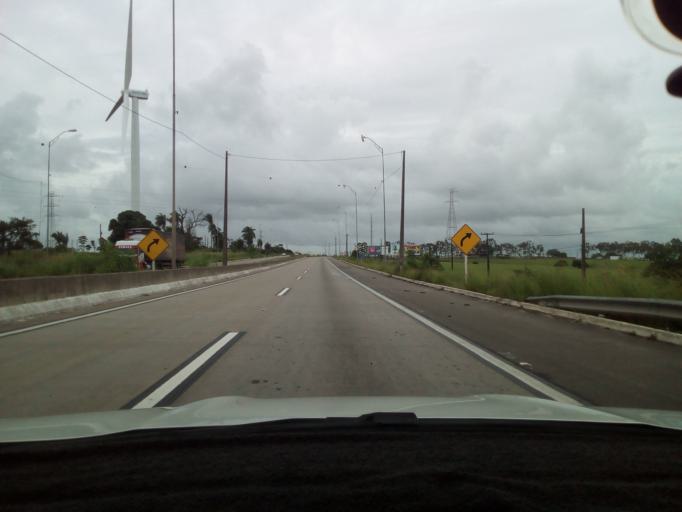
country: BR
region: Paraiba
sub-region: Conde
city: Conde
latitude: -7.2658
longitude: -34.9368
